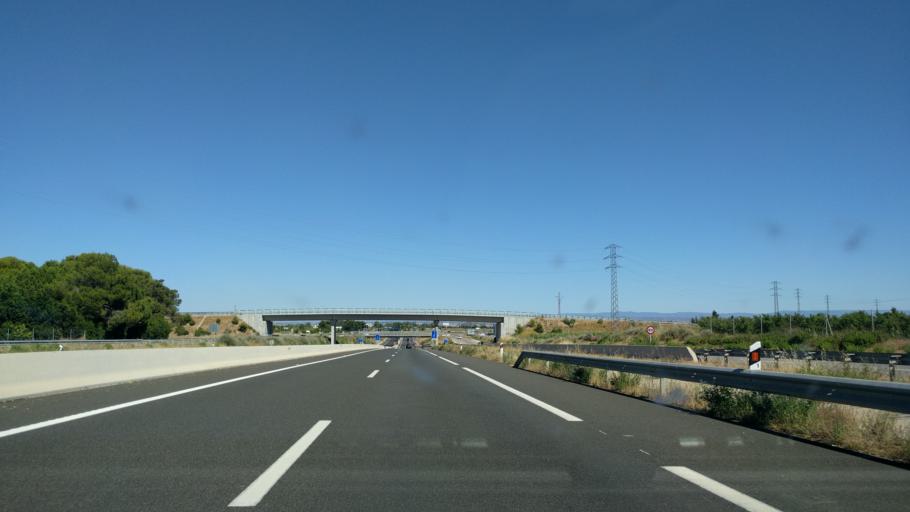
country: ES
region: Catalonia
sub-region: Provincia de Lleida
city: Alpicat
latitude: 41.6506
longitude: 0.5545
